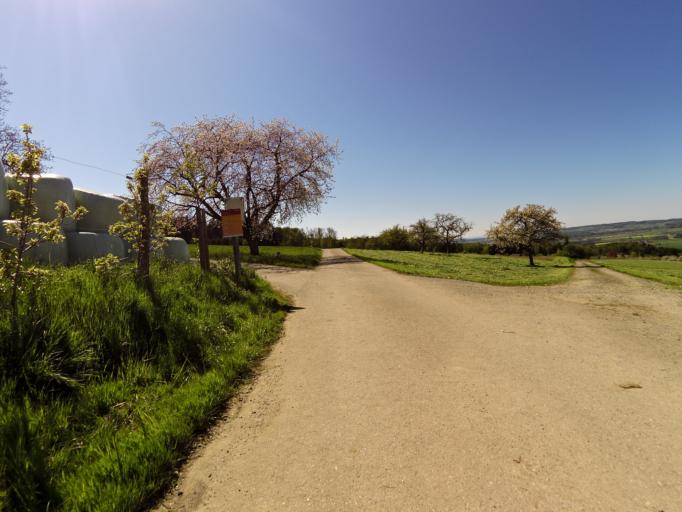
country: CH
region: Thurgau
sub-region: Weinfelden District
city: Weinfelden
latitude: 47.5861
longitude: 9.1167
